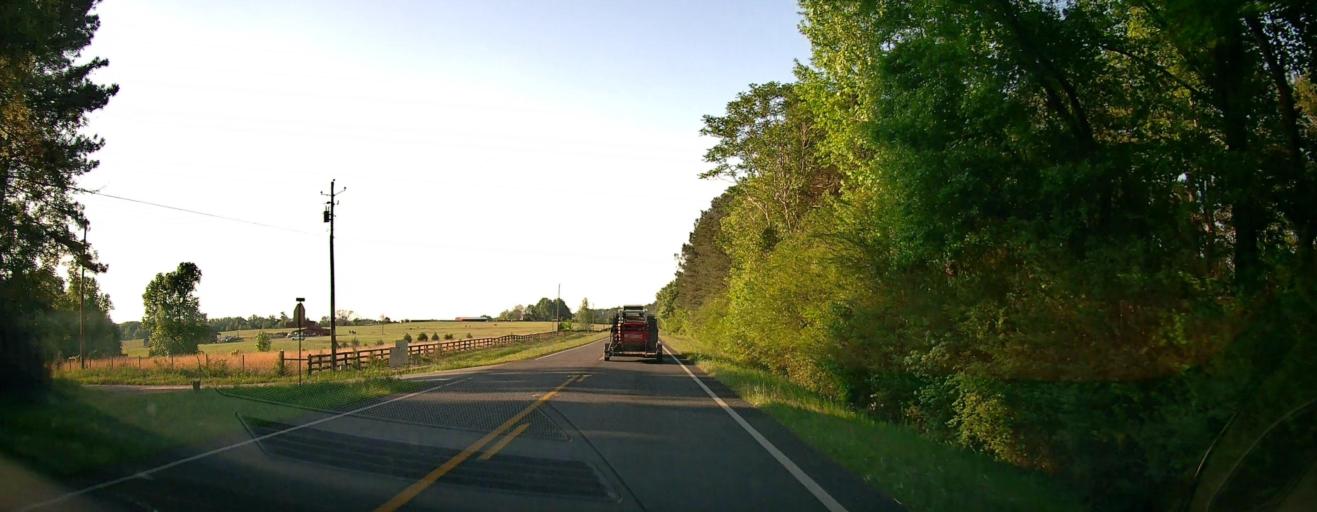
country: US
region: Georgia
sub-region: Jasper County
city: Monticello
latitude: 33.4311
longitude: -83.6192
